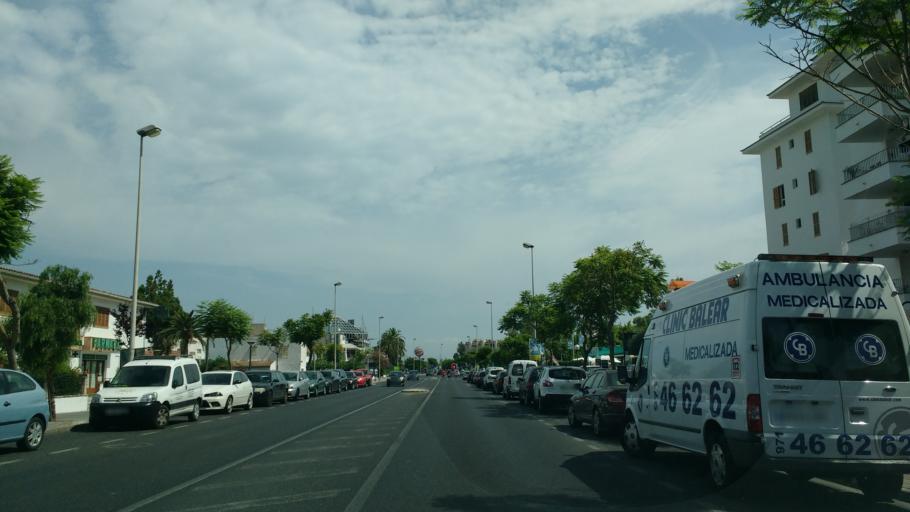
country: ES
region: Balearic Islands
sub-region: Illes Balears
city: Port d'Alcudia
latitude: 39.8377
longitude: 3.1197
